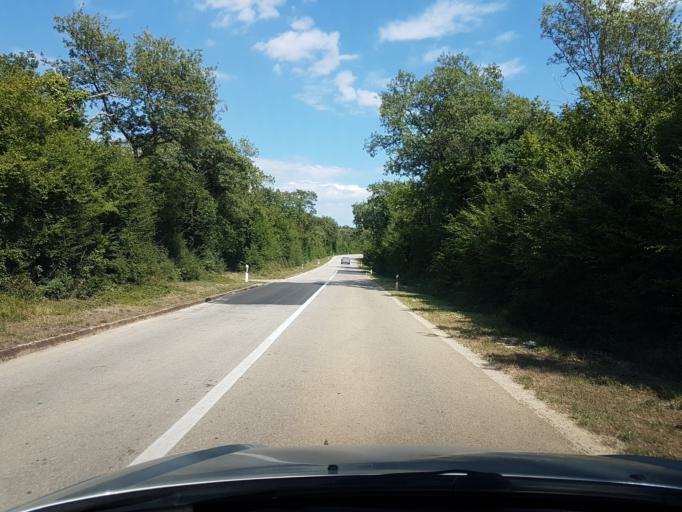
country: HR
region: Istarska
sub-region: Grad Rovinj
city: Rovinj
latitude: 45.1413
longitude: 13.7072
